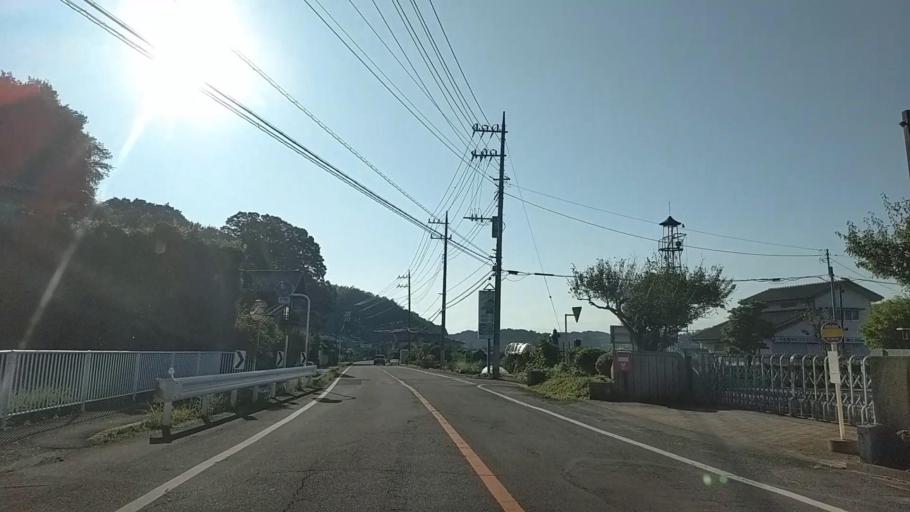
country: JP
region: Gunma
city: Annaka
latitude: 36.3525
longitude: 138.8646
